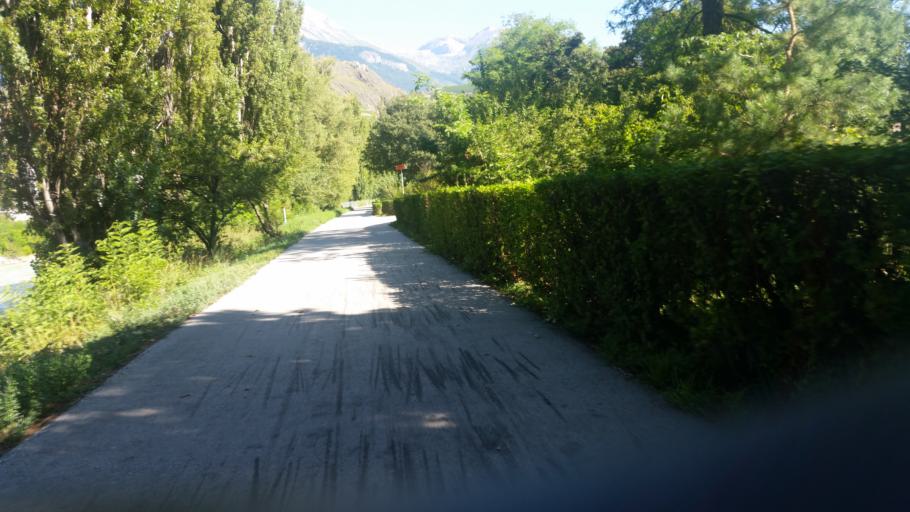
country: CH
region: Valais
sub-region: Sion District
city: Sitten
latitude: 46.2293
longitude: 7.3704
